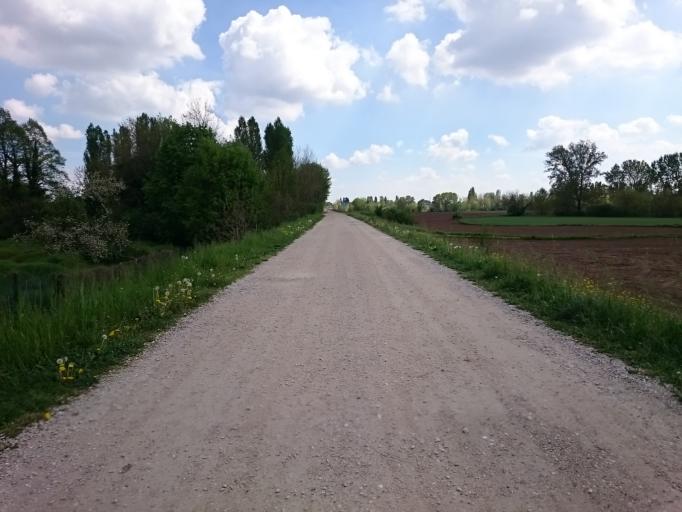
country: IT
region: Veneto
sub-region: Provincia di Padova
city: Selvazzano Dentro
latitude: 45.3966
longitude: 11.7951
